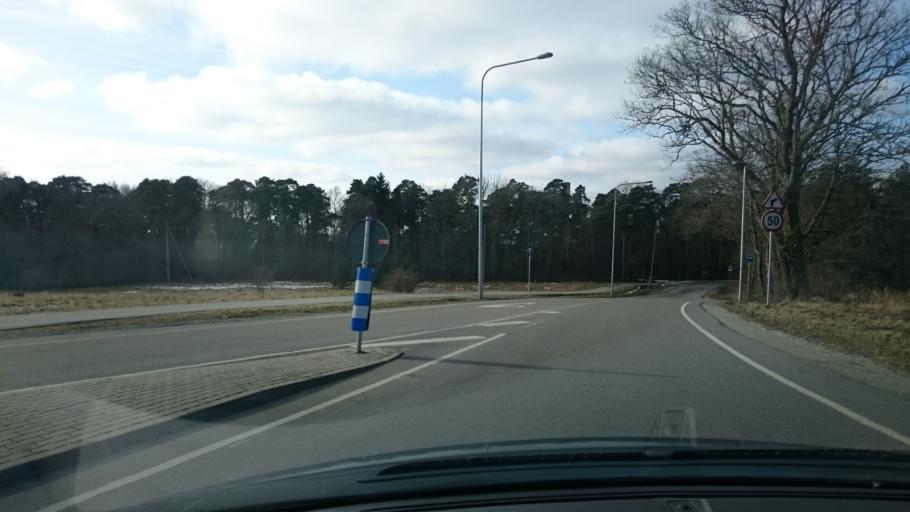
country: EE
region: Harju
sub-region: Paldiski linn
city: Paldiski
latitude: 59.3774
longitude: 24.2387
